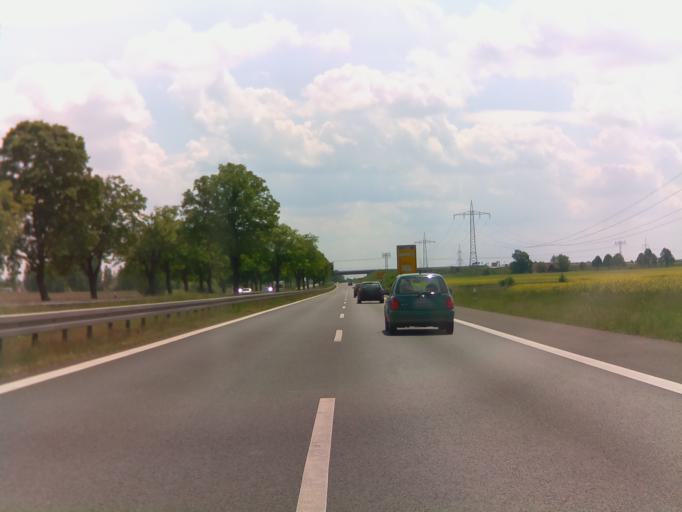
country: DE
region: Brandenburg
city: Wustermark
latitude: 52.5653
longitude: 12.9208
